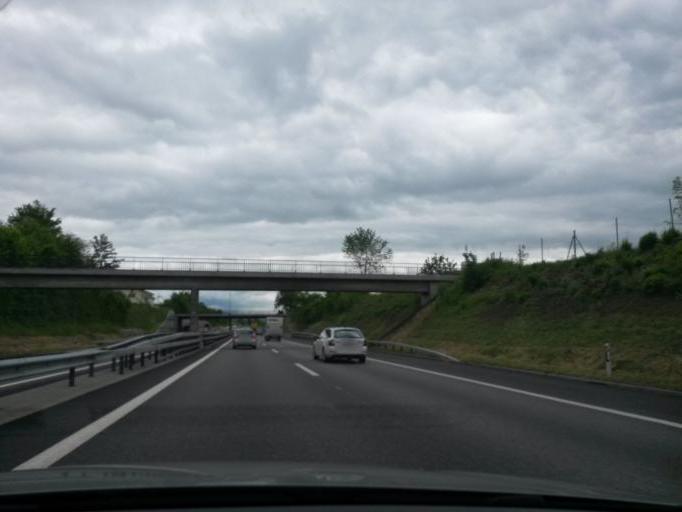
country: CH
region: Aargau
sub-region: Bezirk Zofingen
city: Brittnau
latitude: 47.2581
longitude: 7.9506
